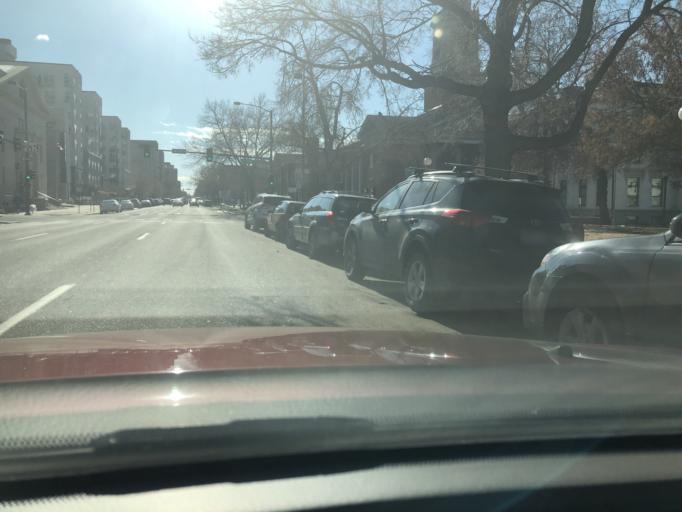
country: US
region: Colorado
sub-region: Denver County
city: Denver
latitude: 39.7389
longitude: -104.9836
